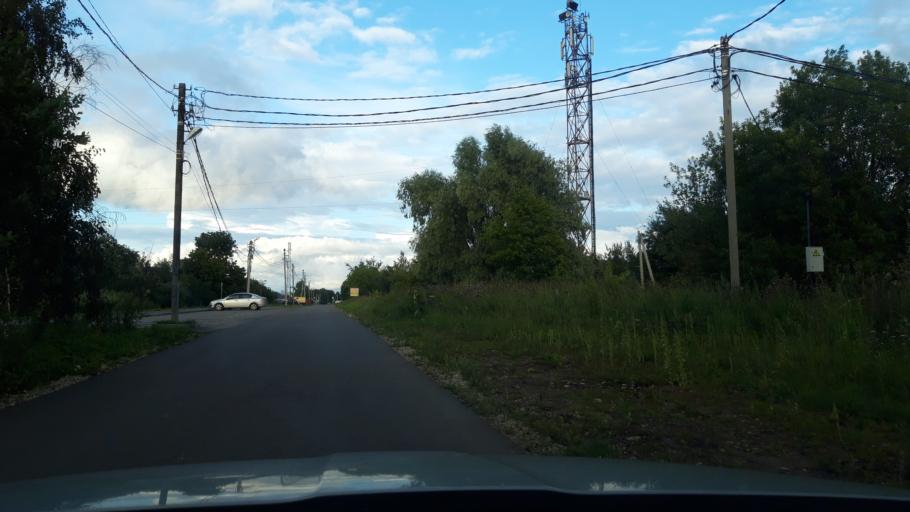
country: RU
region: Moskovskaya
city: Povarovo
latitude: 56.0201
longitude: 36.9989
